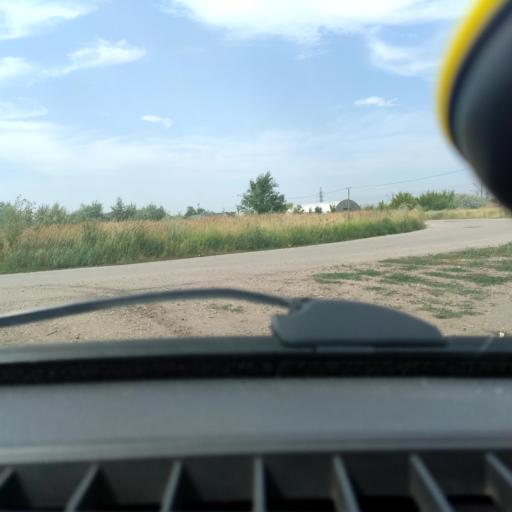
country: RU
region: Samara
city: Tol'yatti
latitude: 53.5609
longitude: 49.3444
